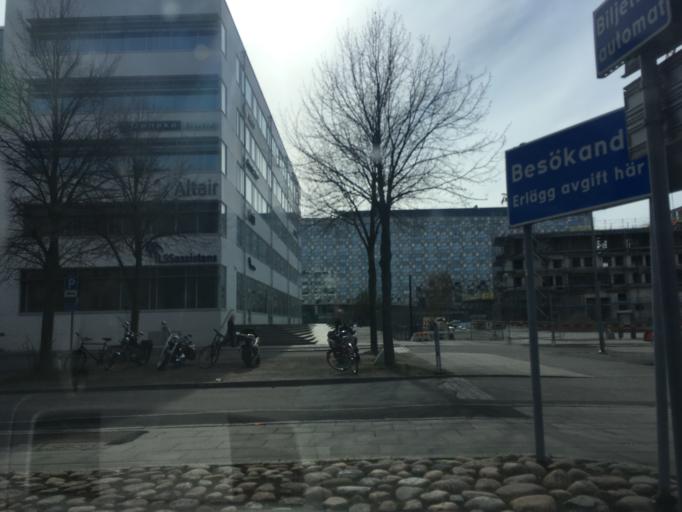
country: SE
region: Vaestra Goetaland
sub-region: Goteborg
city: Goeteborg
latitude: 57.7083
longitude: 11.9436
